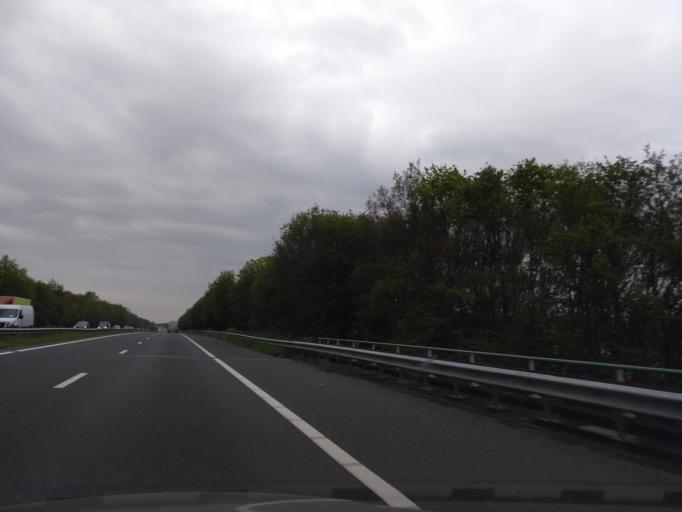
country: NL
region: Overijssel
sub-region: Gemeente Steenwijkerland
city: Steenwijkerwold
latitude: 52.8296
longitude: 6.0639
